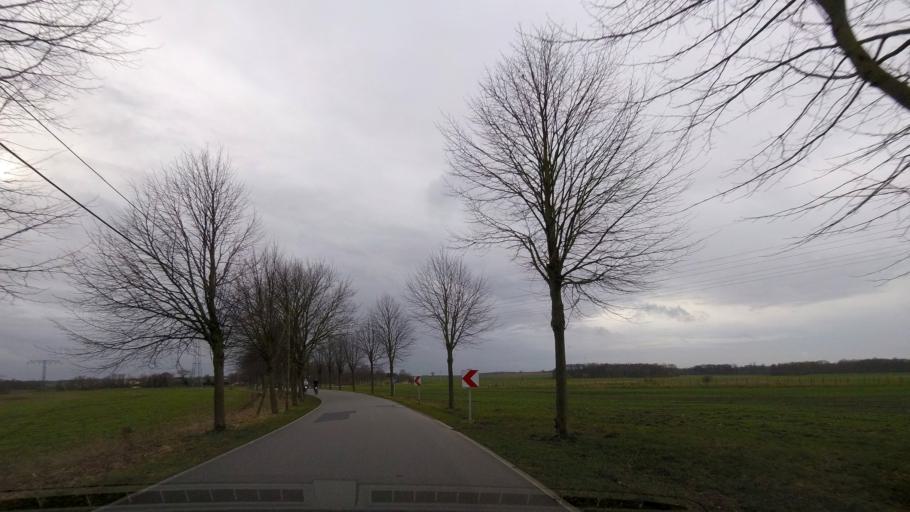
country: DE
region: Mecklenburg-Vorpommern
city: Robel
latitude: 53.4312
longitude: 12.5772
